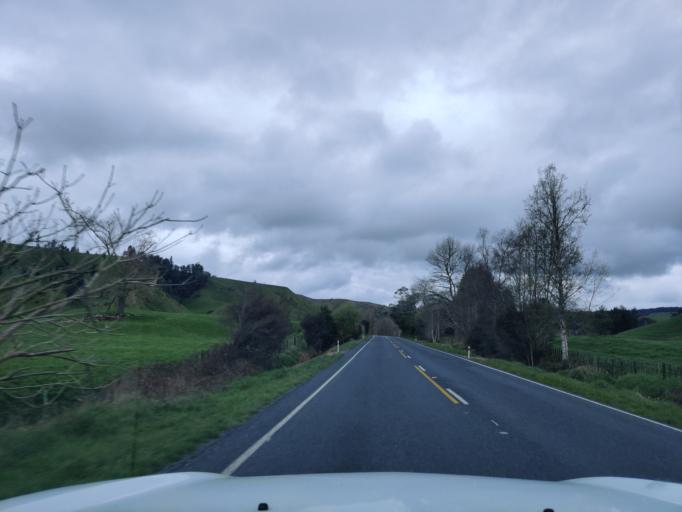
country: NZ
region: Waikato
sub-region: Otorohanga District
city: Otorohanga
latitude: -38.5205
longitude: 175.1858
